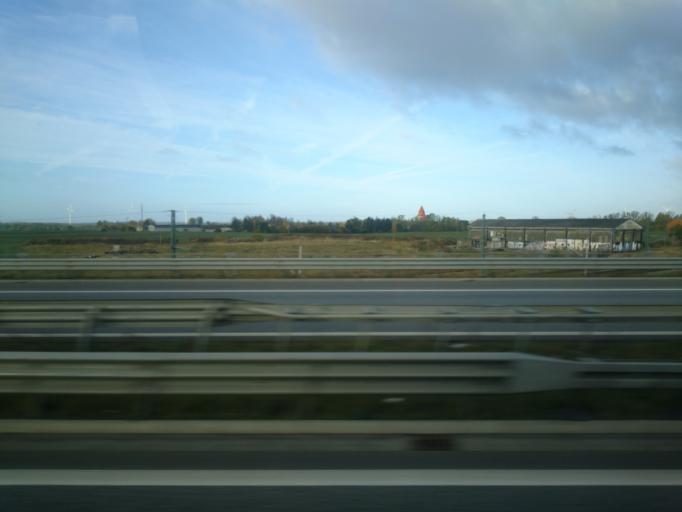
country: DE
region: Mecklenburg-Vorpommern
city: Kavelstorf
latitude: 54.0033
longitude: 12.2027
